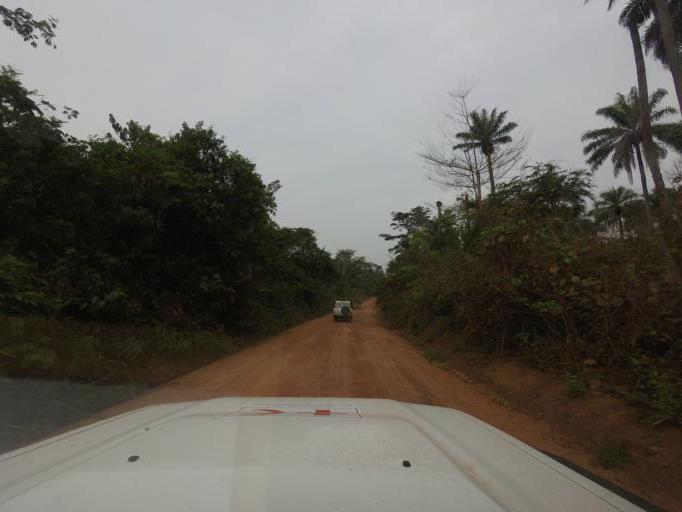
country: LR
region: Lofa
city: Voinjama
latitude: 8.3840
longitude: -9.8303
